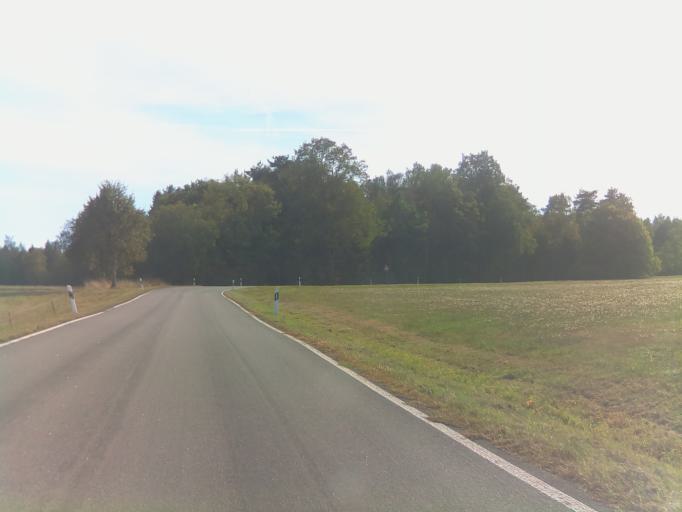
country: DE
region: Thuringia
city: Oberkatz
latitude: 50.5559
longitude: 10.2256
